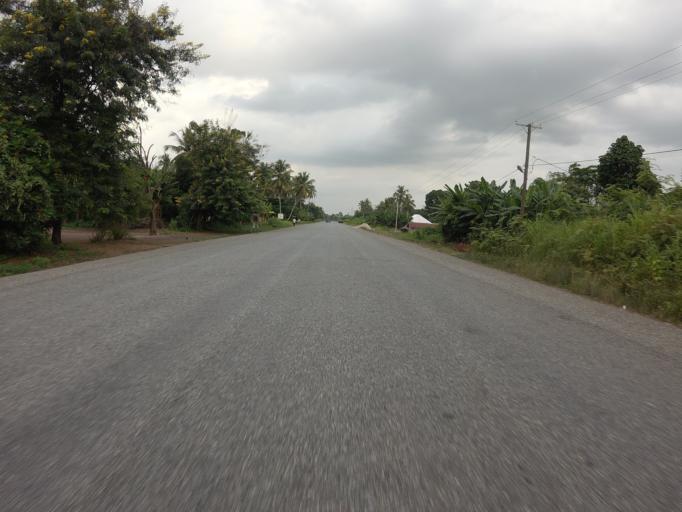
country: GH
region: Volta
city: Ho
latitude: 6.4852
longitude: 0.4914
